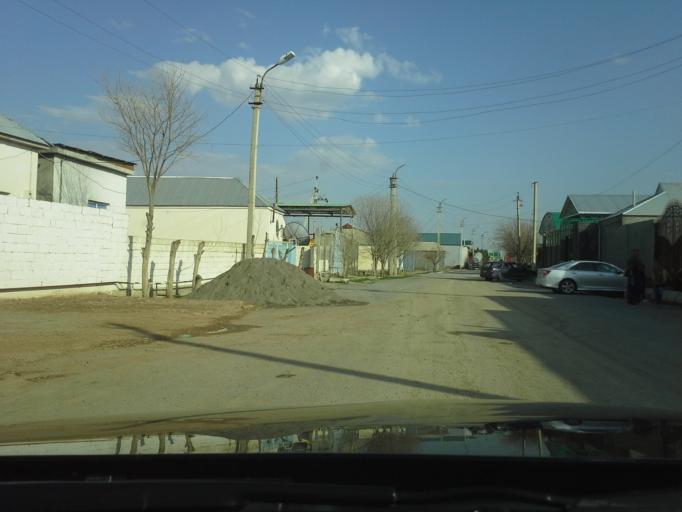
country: TM
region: Ahal
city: Abadan
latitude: 38.0142
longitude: 58.2299
